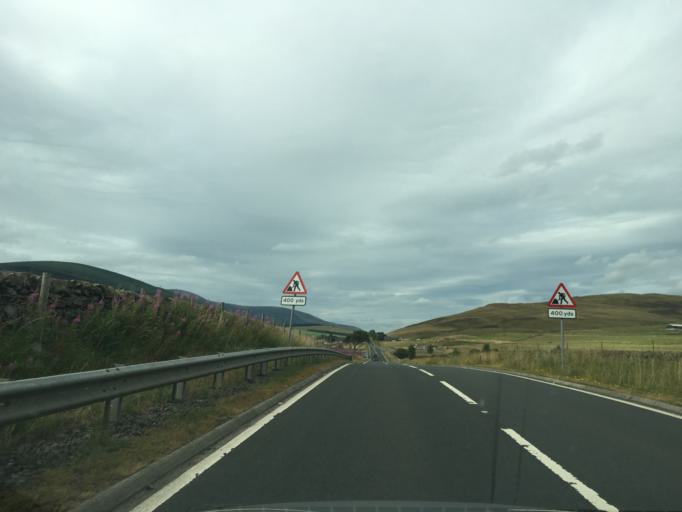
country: GB
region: Scotland
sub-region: South Lanarkshire
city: Biggar
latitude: 55.5289
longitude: -3.6697
